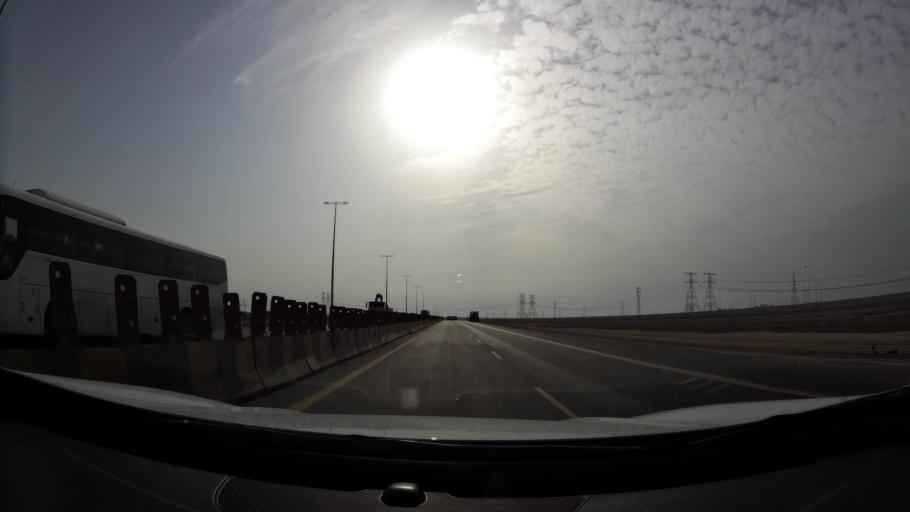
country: AE
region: Abu Dhabi
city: Abu Dhabi
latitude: 24.2244
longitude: 54.4395
